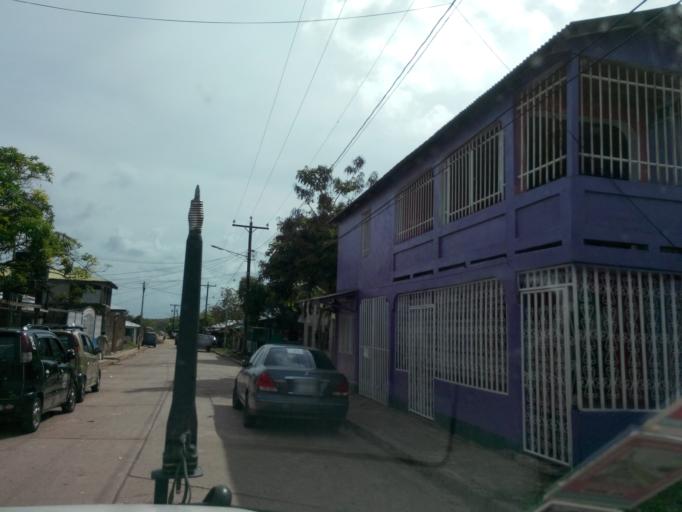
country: NI
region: Atlantico Sur
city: Bluefields
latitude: 11.9960
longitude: -83.7701
